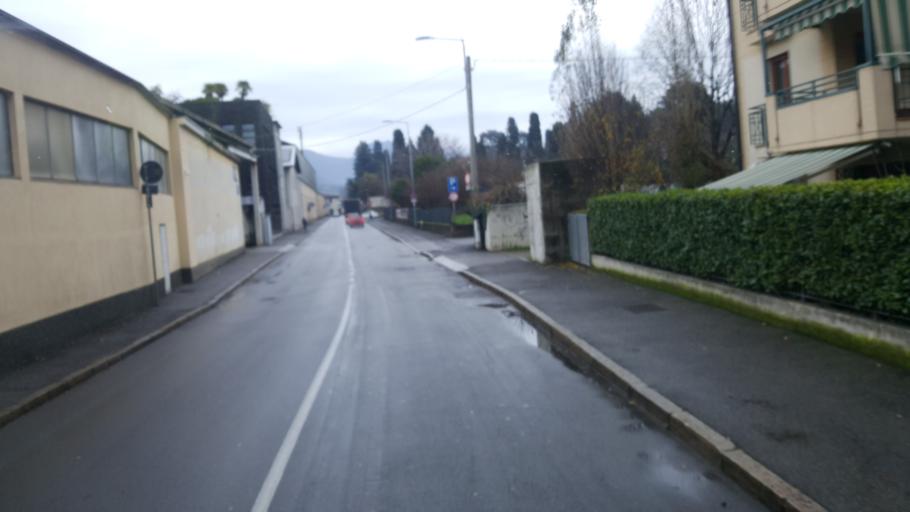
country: IT
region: Lombardy
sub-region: Provincia di Bergamo
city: Bergamo
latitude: 45.6977
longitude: 9.6871
